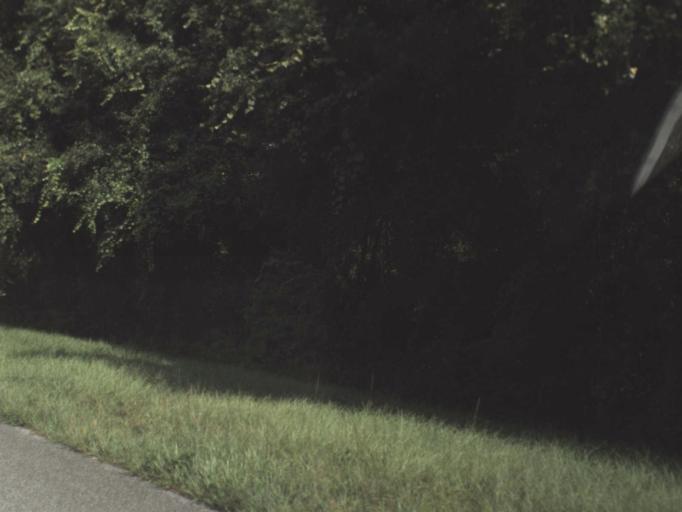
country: US
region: Florida
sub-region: Hernando County
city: Ridge Manor
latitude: 28.5077
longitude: -82.1460
